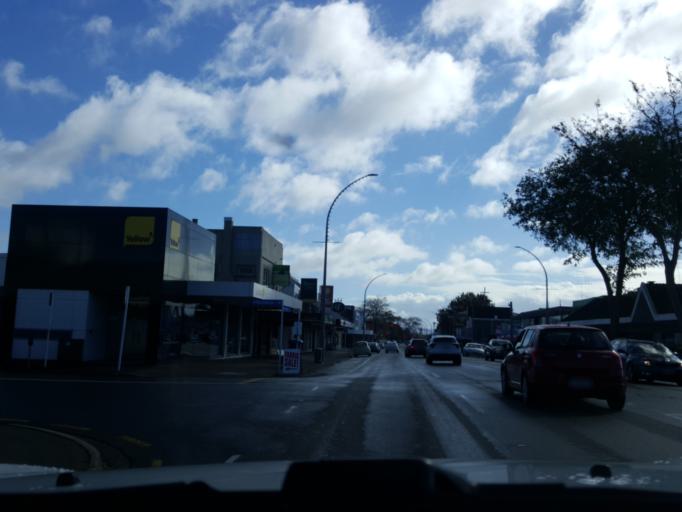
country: NZ
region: Waikato
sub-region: Hamilton City
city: Hamilton
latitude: -37.7817
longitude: 175.2778
